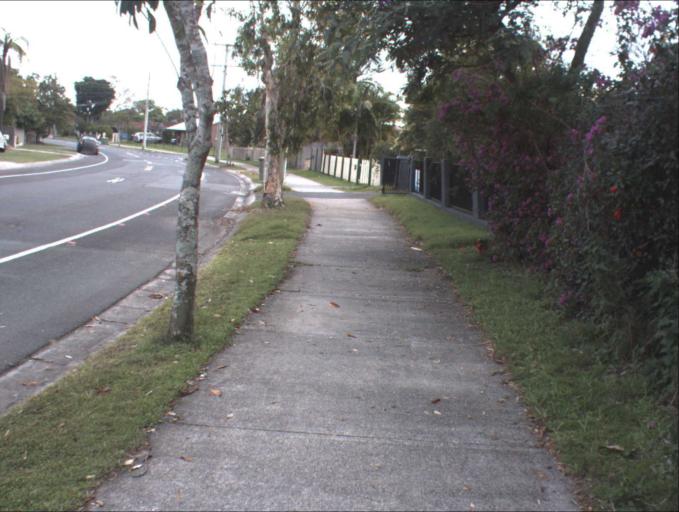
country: AU
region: Queensland
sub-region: Logan
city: Waterford West
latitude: -27.6840
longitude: 153.1480
